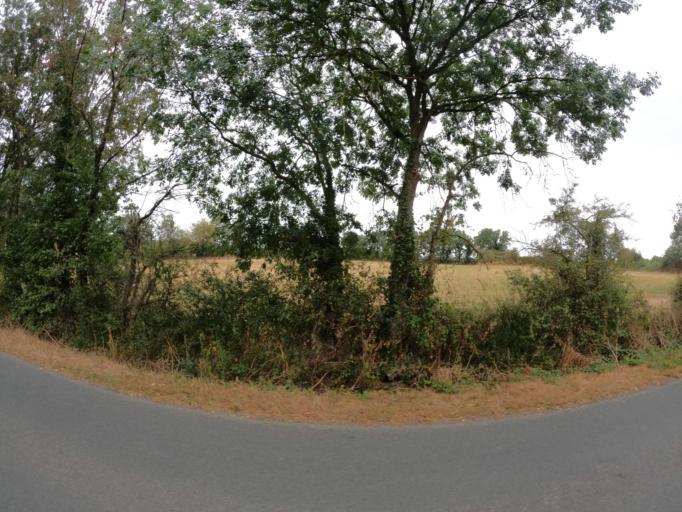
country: FR
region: Pays de la Loire
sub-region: Departement de la Vendee
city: Les Landes-Genusson
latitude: 46.9700
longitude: -1.1146
